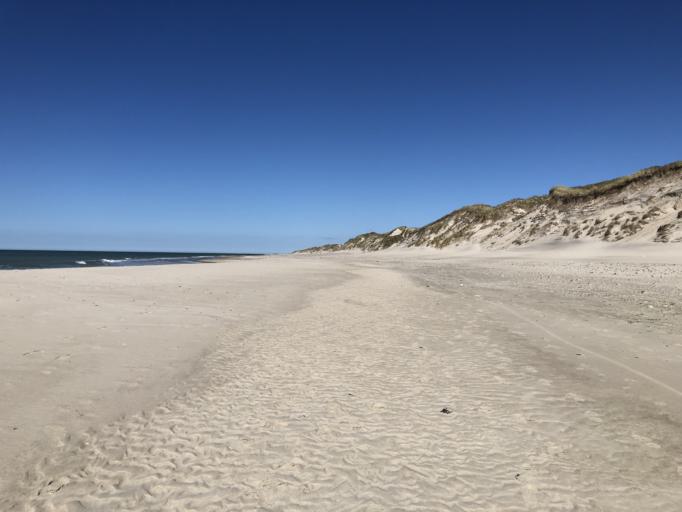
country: DK
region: Central Jutland
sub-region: Holstebro Kommune
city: Ulfborg
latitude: 56.3065
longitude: 8.1230
